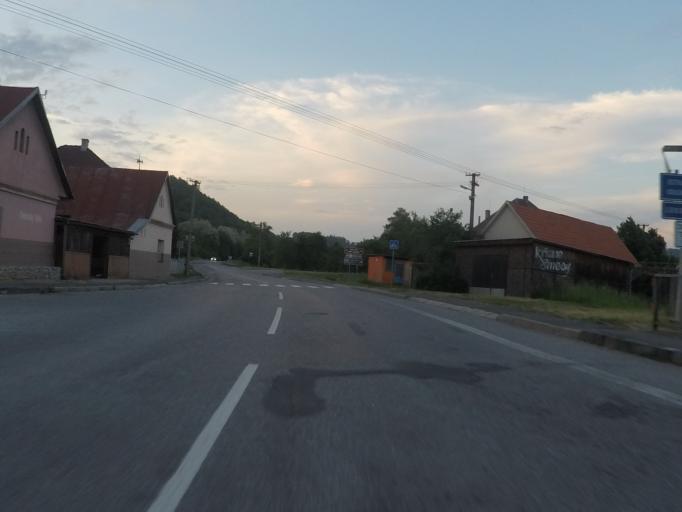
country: SK
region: Banskobystricky
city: Rimavska Sobota
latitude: 48.5126
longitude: 19.9424
